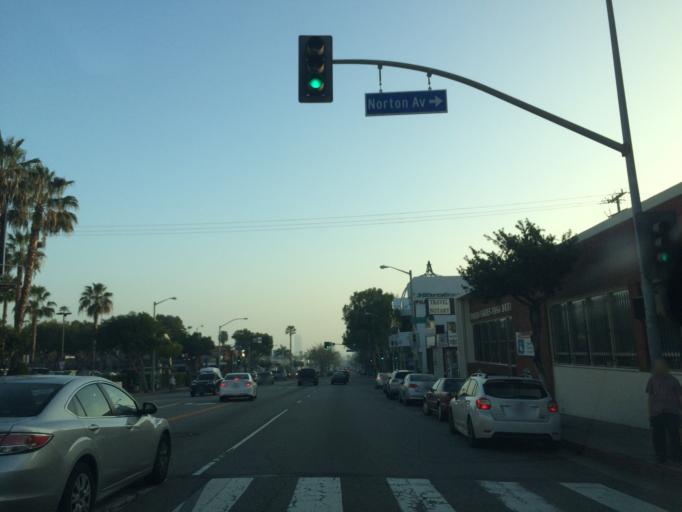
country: US
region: California
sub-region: Los Angeles County
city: West Hollywood
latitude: 34.0919
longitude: -118.3616
